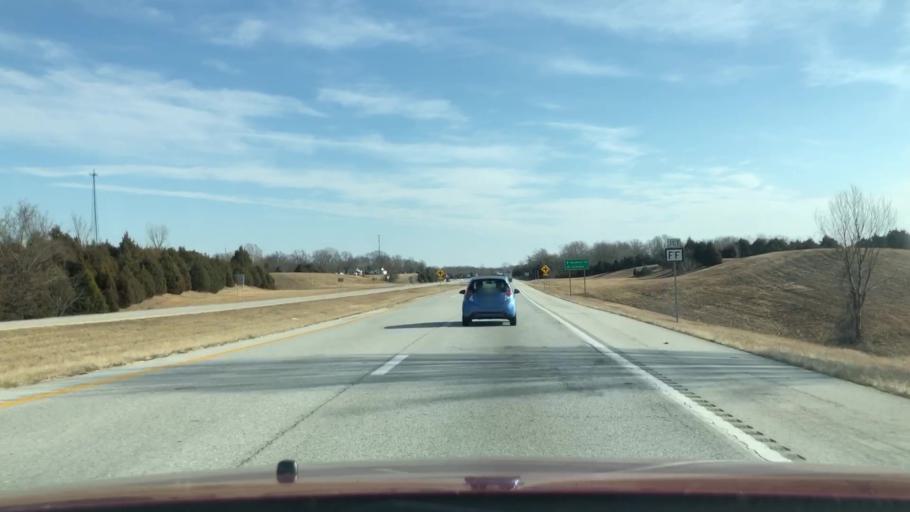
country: US
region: Missouri
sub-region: Webster County
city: Rogersville
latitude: 37.1514
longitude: -92.9467
